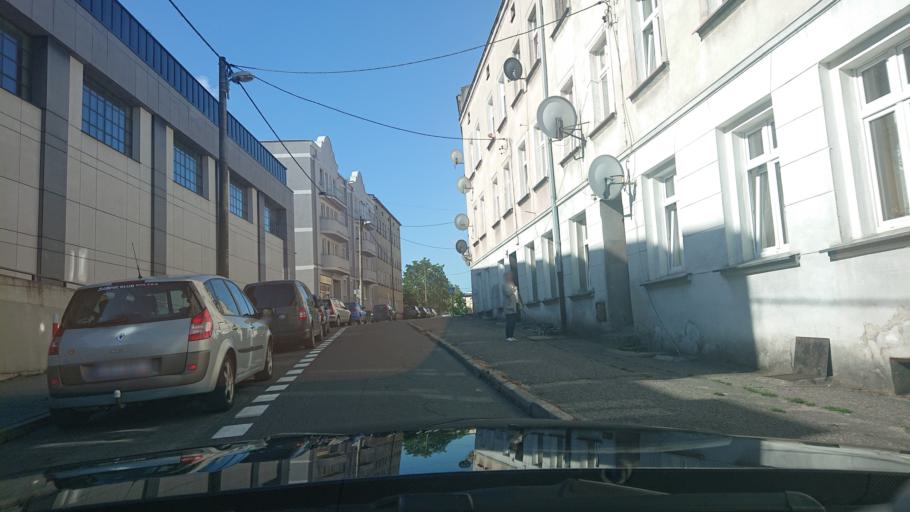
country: PL
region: Greater Poland Voivodeship
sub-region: Powiat gnieznienski
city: Gniezno
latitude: 52.5401
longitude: 17.5968
